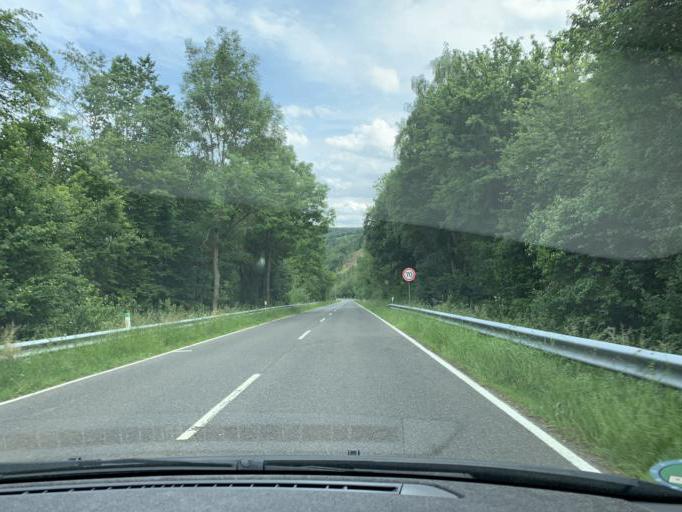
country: DE
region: North Rhine-Westphalia
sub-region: Regierungsbezirk Koln
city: Hurtgenwald
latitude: 50.6831
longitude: 6.4098
